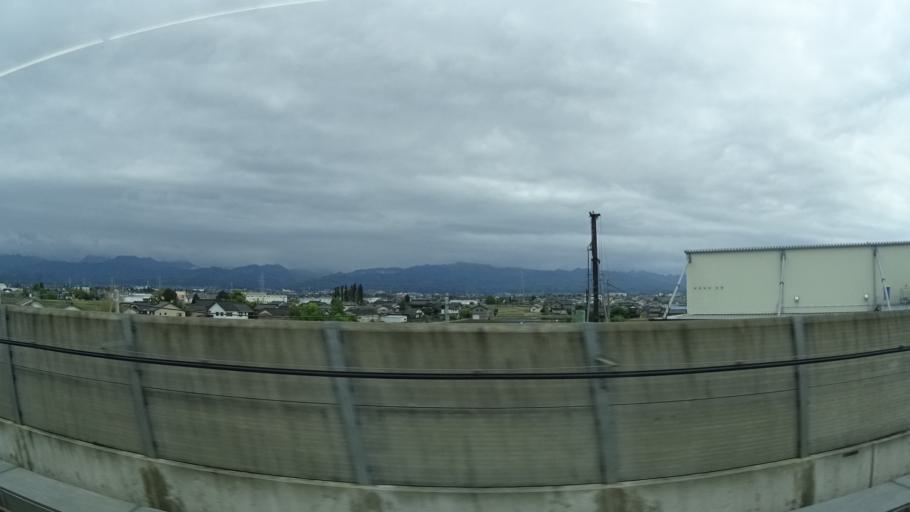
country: JP
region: Toyama
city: Namerikawa
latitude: 36.7223
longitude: 137.3222
